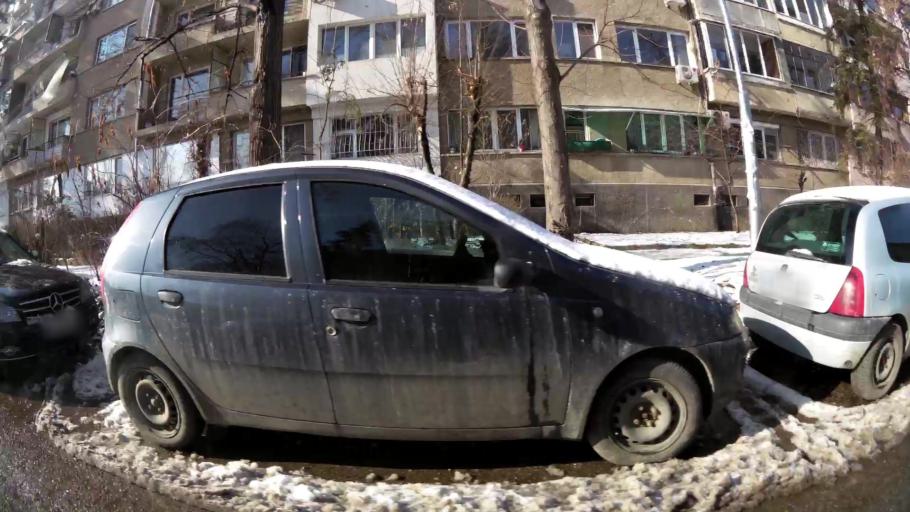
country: BG
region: Sofia-Capital
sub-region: Stolichna Obshtina
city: Sofia
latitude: 42.6762
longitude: 23.3111
